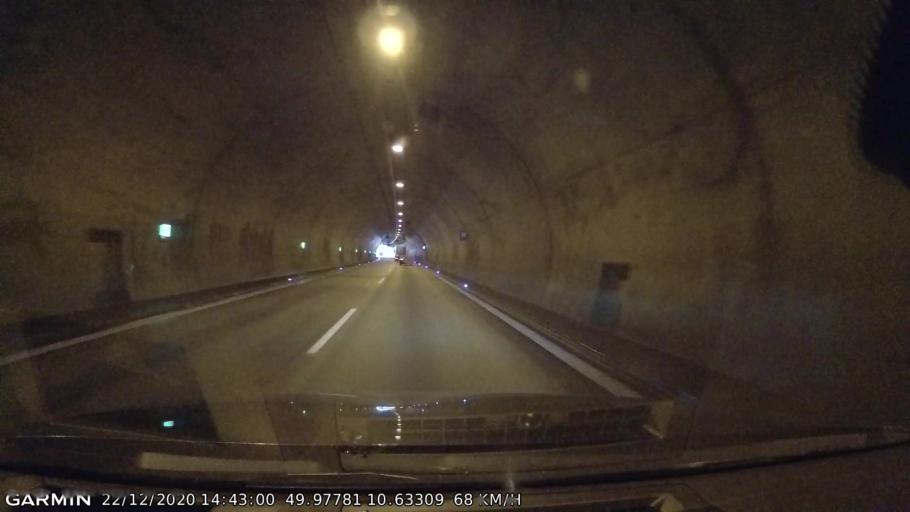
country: DE
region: Bavaria
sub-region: Regierungsbezirk Unterfranken
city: Eltmann
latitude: 49.9778
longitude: 10.6330
